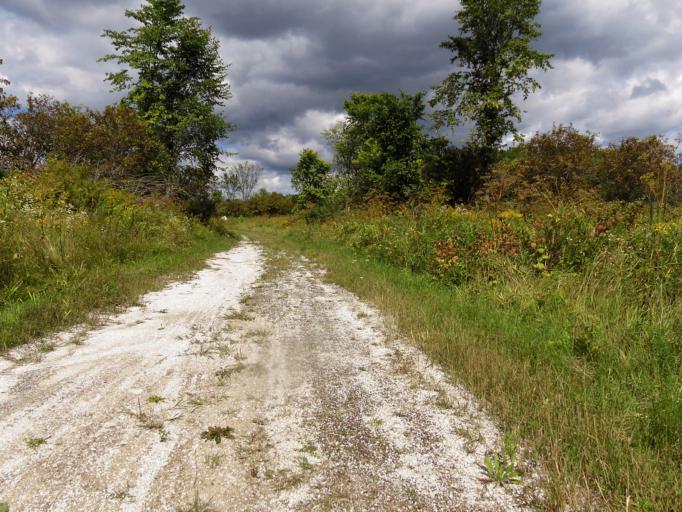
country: CA
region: Quebec
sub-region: Outaouais
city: Wakefield
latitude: 45.8346
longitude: -75.9775
